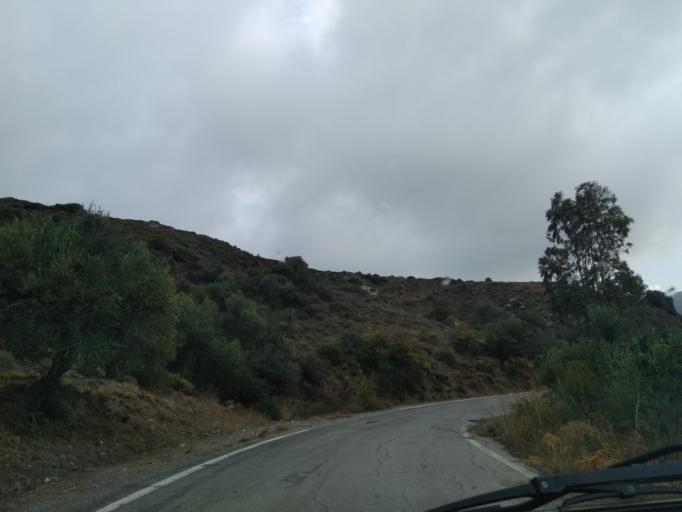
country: GR
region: Crete
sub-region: Nomos Lasithiou
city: Siteia
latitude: 35.1469
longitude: 26.0212
